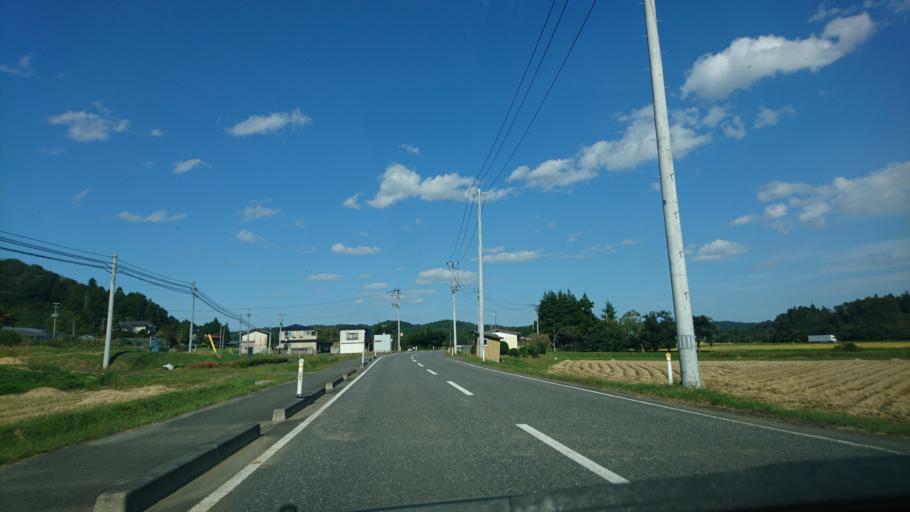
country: JP
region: Iwate
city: Ichinoseki
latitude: 38.8381
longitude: 141.0148
